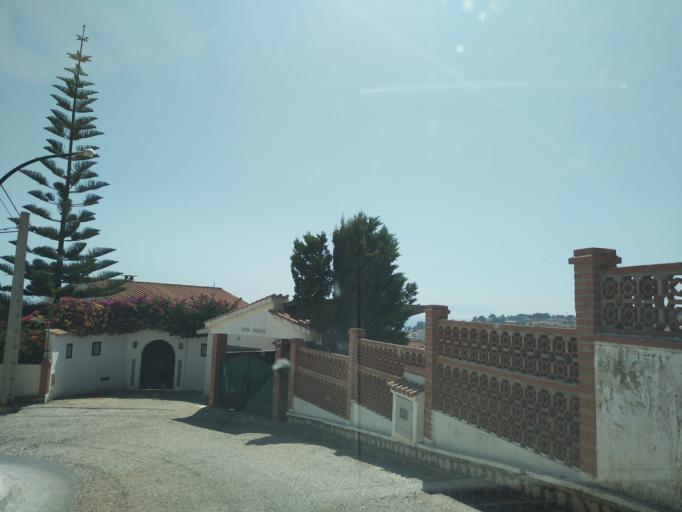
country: ES
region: Andalusia
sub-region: Provincia de Malaga
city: Valdes
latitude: 36.7184
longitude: -4.1915
